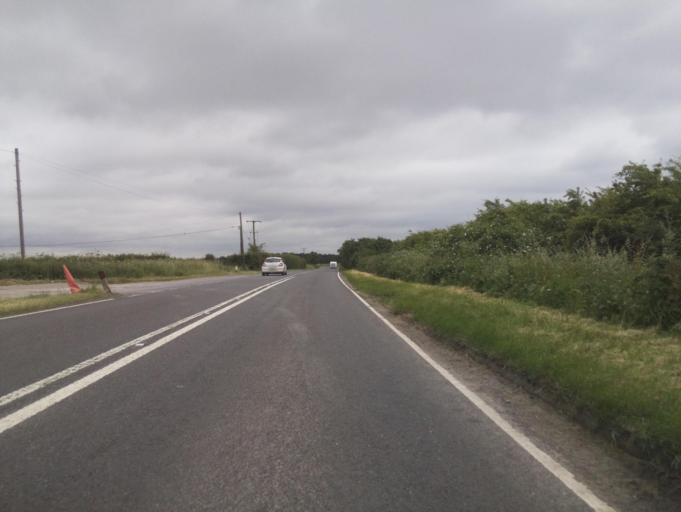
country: GB
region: England
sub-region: Nottinghamshire
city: East Leake
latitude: 52.8168
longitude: -1.1984
